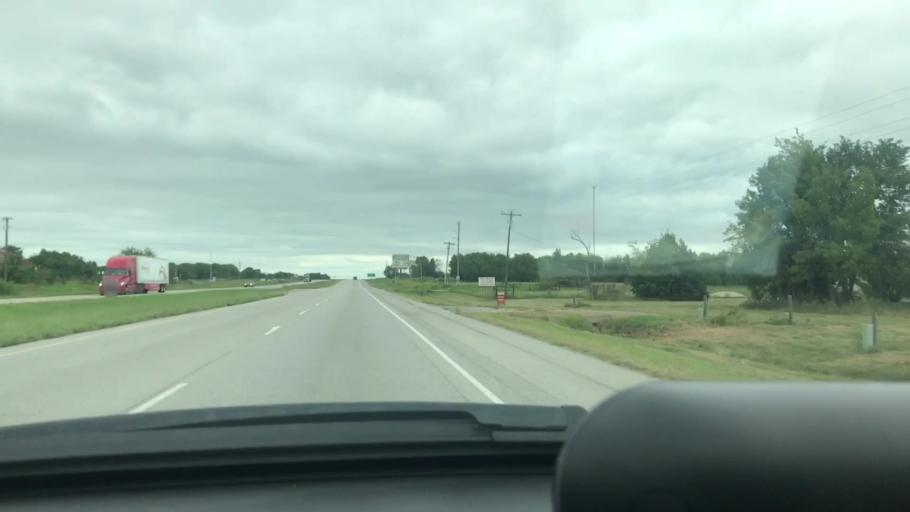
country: US
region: Oklahoma
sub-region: Mayes County
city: Chouteau
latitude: 36.1029
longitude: -95.3614
